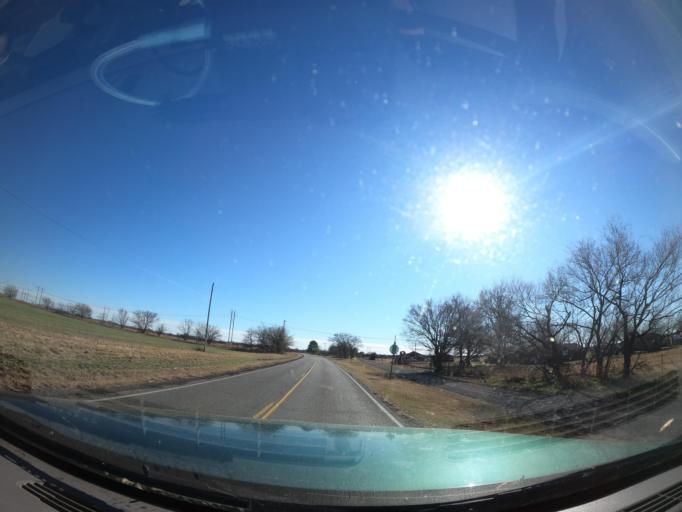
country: US
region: Oklahoma
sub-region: McIntosh County
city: Checotah
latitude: 35.5778
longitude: -95.6598
